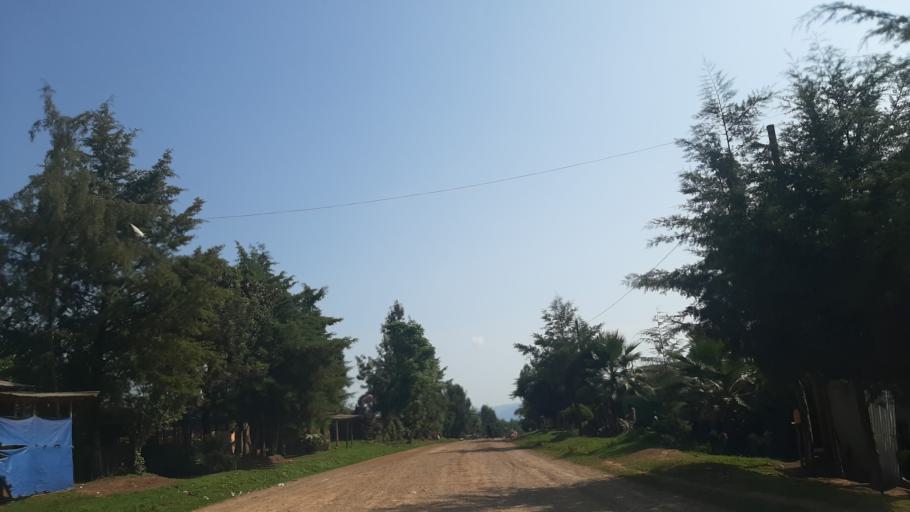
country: ET
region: Oromiya
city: Jima
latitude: 7.7923
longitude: 36.8012
